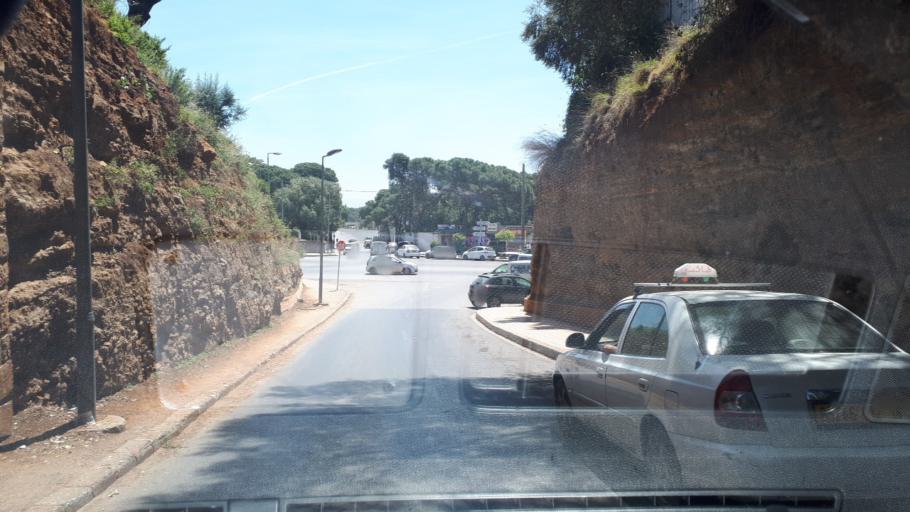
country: DZ
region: Alger
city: Algiers
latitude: 36.7468
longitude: 3.0635
